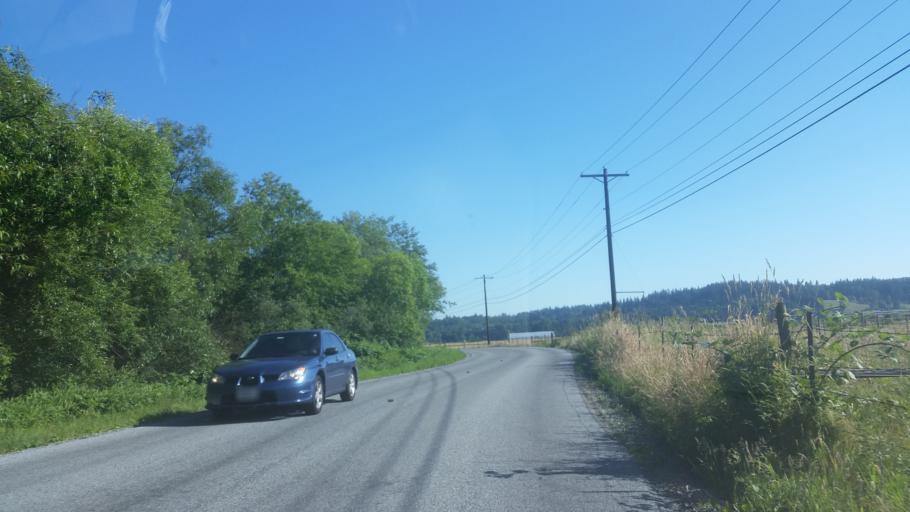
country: US
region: Washington
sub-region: Snohomish County
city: Snohomish
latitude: 47.8942
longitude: -122.1027
